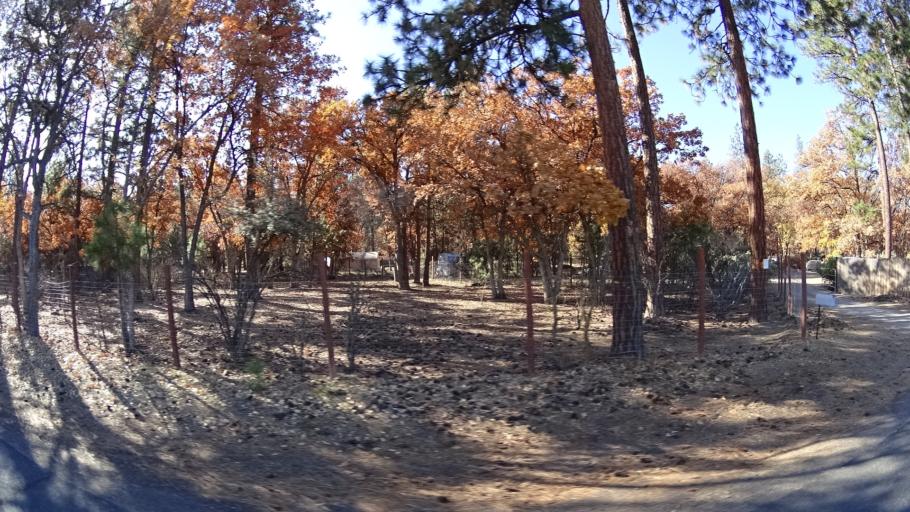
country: US
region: California
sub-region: Siskiyou County
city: Yreka
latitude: 41.6635
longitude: -122.6038
